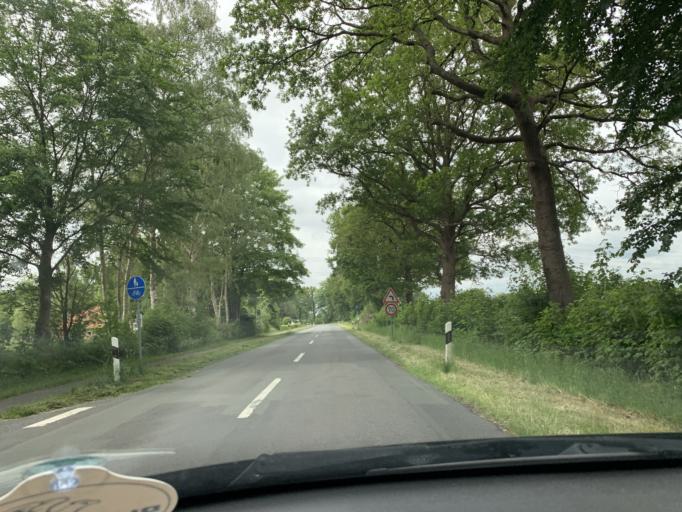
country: DE
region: Lower Saxony
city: Bockhorn
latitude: 53.3474
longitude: 8.0463
